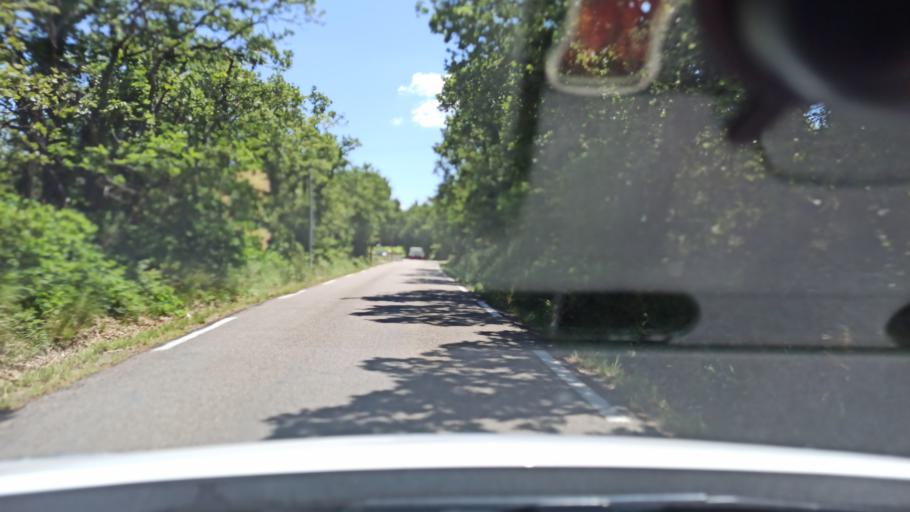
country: FR
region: Provence-Alpes-Cote d'Azur
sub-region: Departement du Vaucluse
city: Caumont-sur-Durance
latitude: 43.9044
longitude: 4.9287
